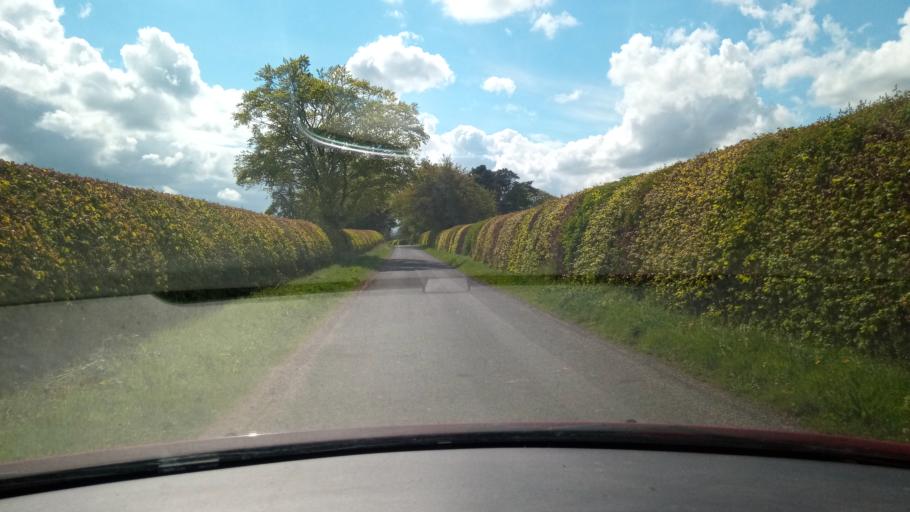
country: GB
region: Scotland
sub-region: The Scottish Borders
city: Saint Boswells
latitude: 55.5575
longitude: -2.6208
